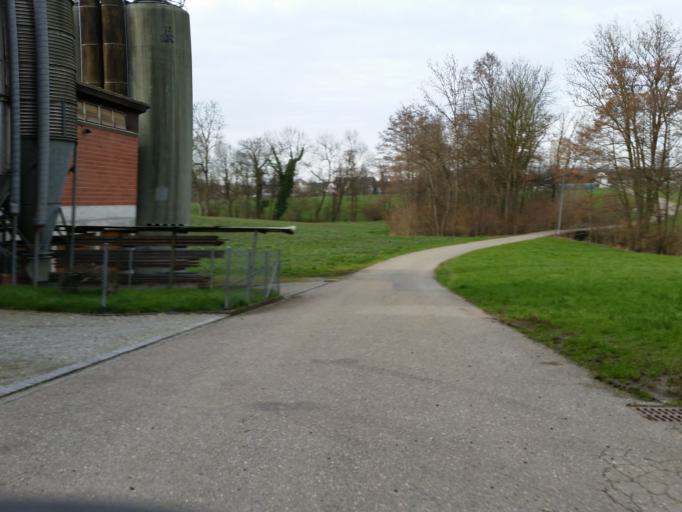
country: CH
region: Thurgau
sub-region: Arbon District
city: Amriswil
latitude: 47.5508
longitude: 9.3266
